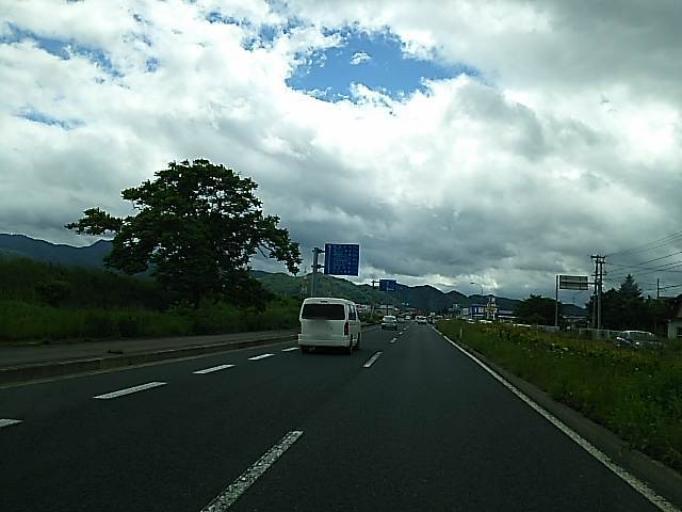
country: JP
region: Iwate
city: Morioka-shi
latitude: 39.7050
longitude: 141.0766
